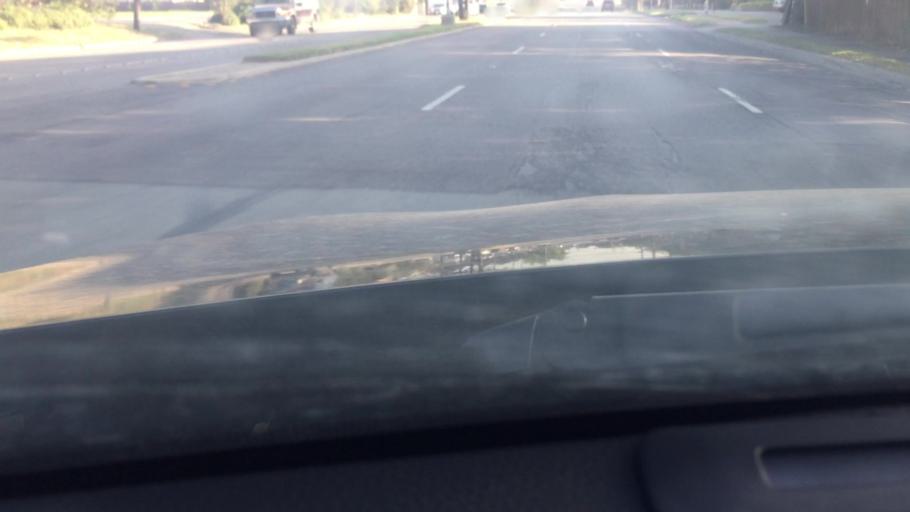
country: US
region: Texas
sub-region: Dallas County
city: Farmers Branch
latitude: 32.9122
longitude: -96.8561
